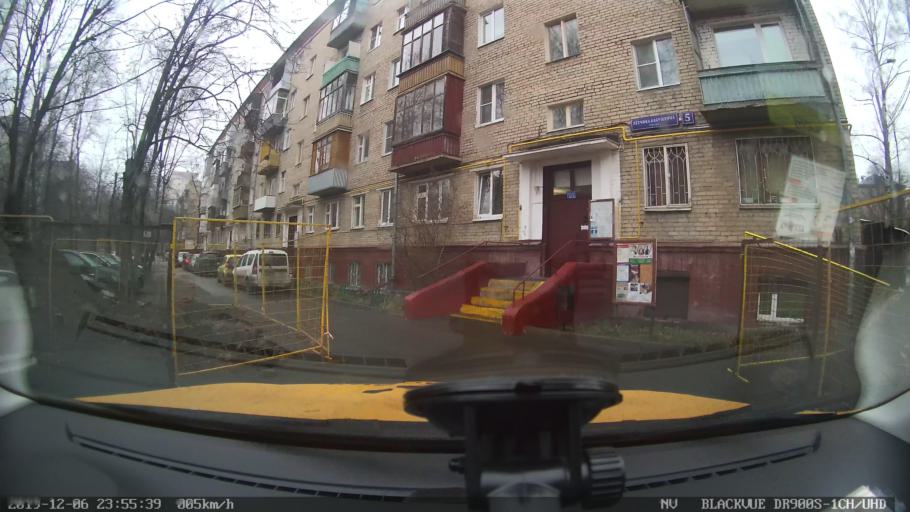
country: RU
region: Moscow
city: Leonovo
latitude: 55.8581
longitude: 37.6722
